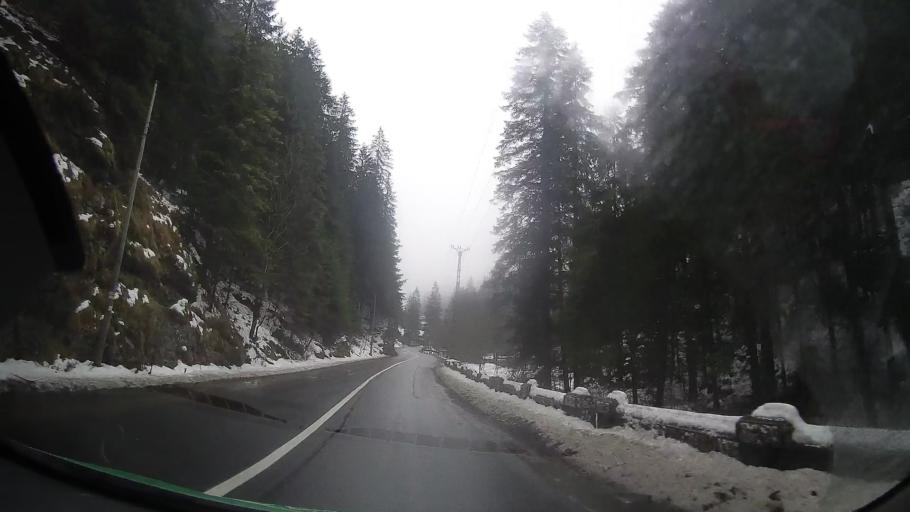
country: RO
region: Neamt
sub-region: Comuna Bicaz Chei
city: Bicaz Chei
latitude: 46.8000
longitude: 25.8008
